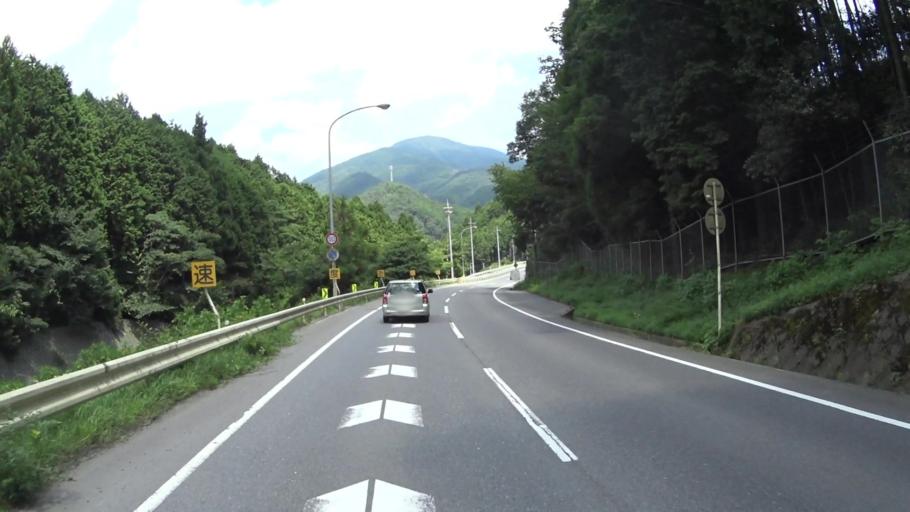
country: JP
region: Shiga Prefecture
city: Kitahama
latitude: 35.1625
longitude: 135.8531
